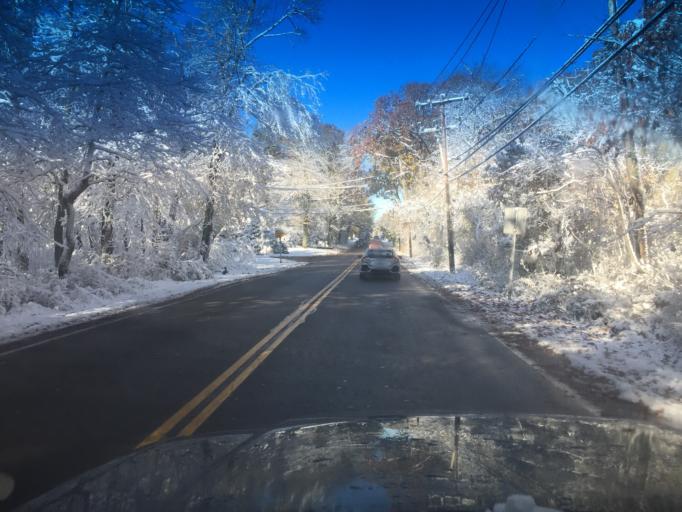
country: US
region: Massachusetts
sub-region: Worcester County
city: Milford
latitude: 42.1458
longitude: -71.4709
